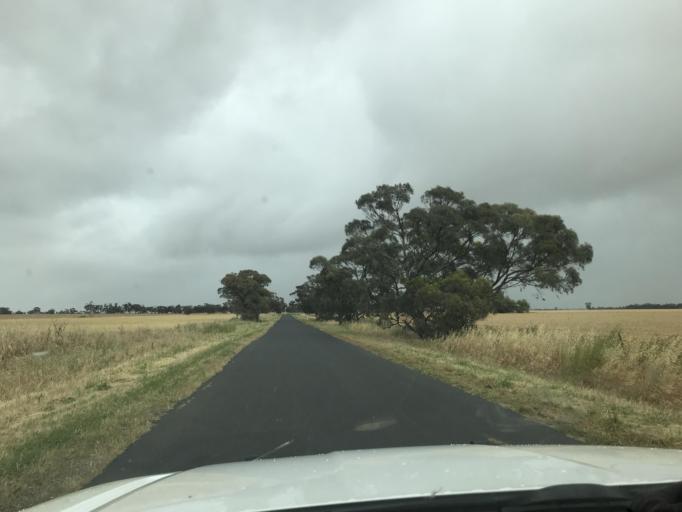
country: AU
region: South Australia
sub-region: Tatiara
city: Bordertown
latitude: -36.3438
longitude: 141.2261
